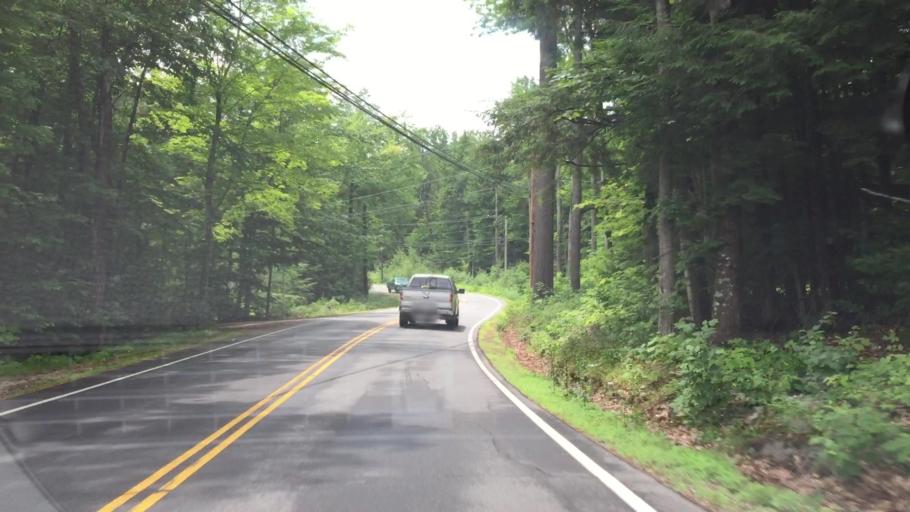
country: US
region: New Hampshire
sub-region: Grafton County
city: Holderness
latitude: 43.7588
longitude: -71.5571
